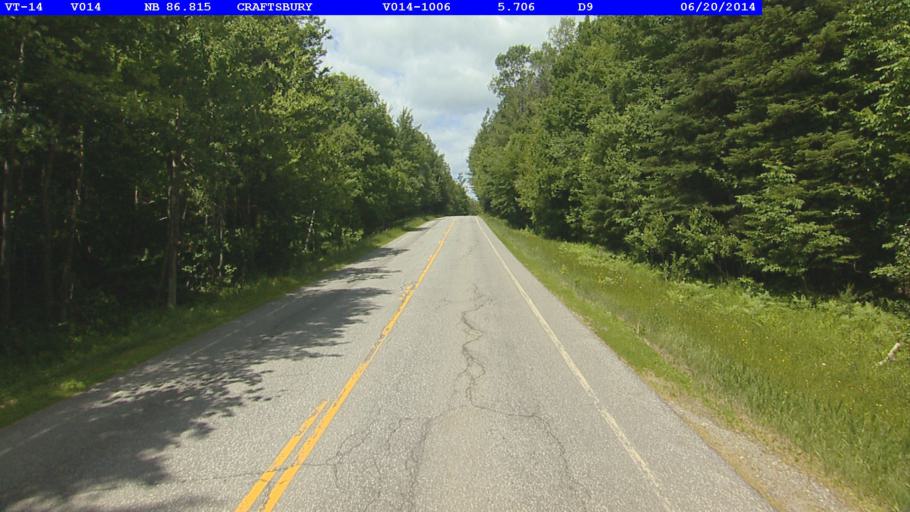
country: US
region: Vermont
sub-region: Caledonia County
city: Hardwick
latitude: 44.6727
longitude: -72.4048
